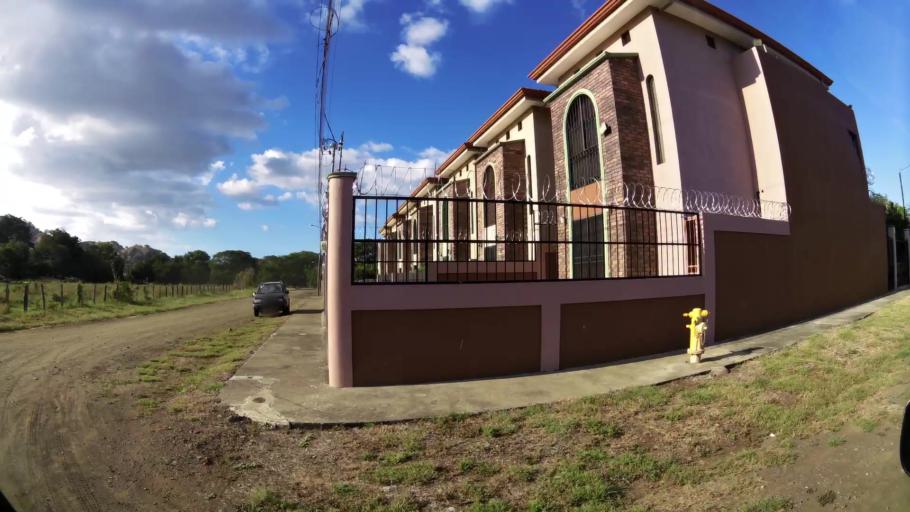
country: CR
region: Guanacaste
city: Sardinal
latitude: 10.5461
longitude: -85.6977
